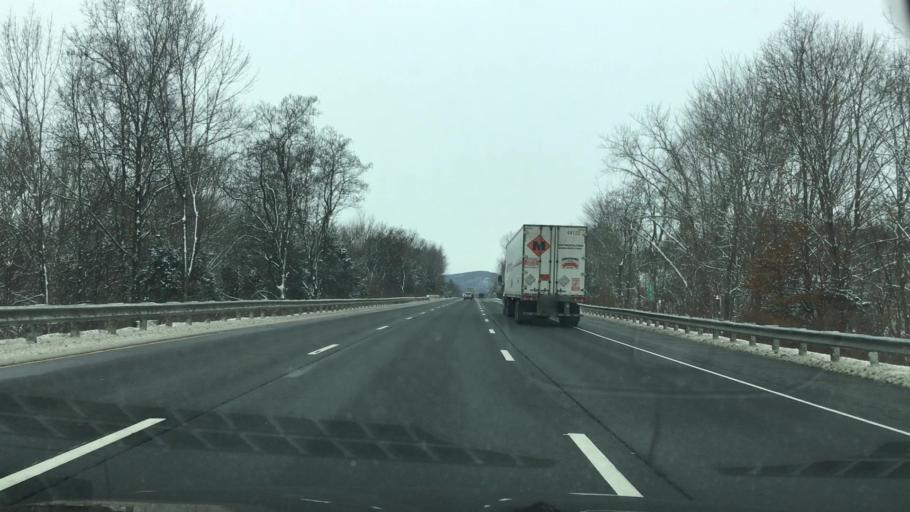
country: US
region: Connecticut
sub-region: Middlesex County
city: Cromwell
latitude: 41.6132
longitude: -72.6986
